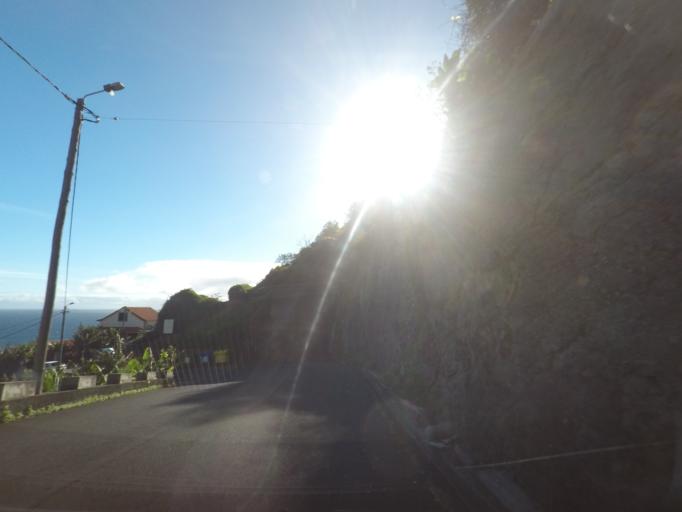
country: PT
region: Madeira
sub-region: Calheta
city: Arco da Calheta
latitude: 32.7050
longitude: -17.1355
